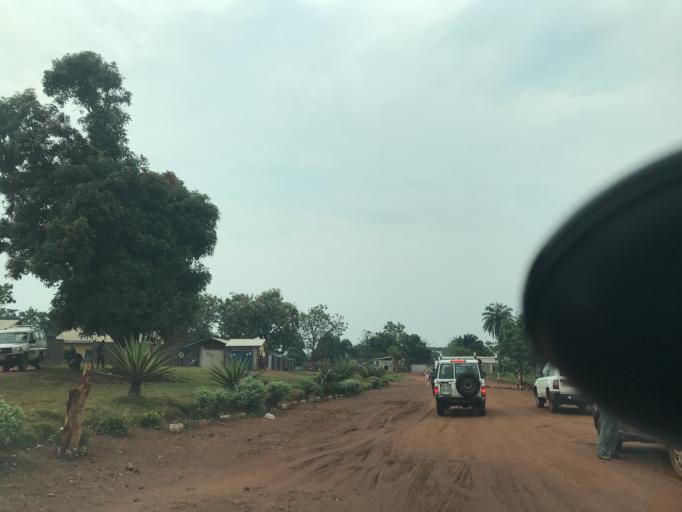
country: CD
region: Equateur
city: Gemena
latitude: 3.2466
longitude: 19.7830
